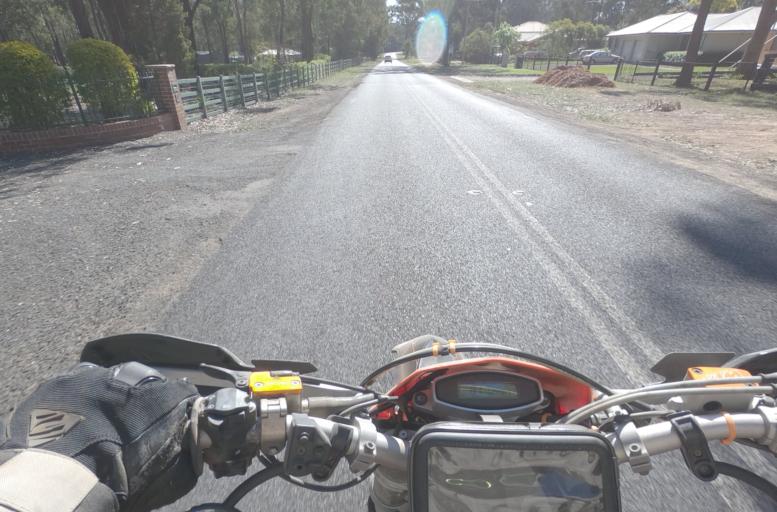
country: AU
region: New South Wales
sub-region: Hawkesbury
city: Scheyville
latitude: -33.5819
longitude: 150.8810
